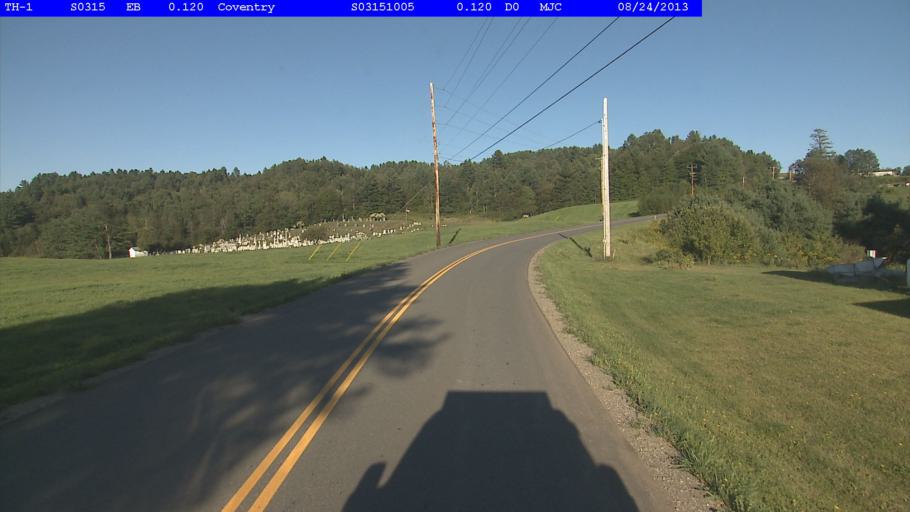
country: US
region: Vermont
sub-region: Orleans County
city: Newport
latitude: 44.8682
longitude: -72.2579
